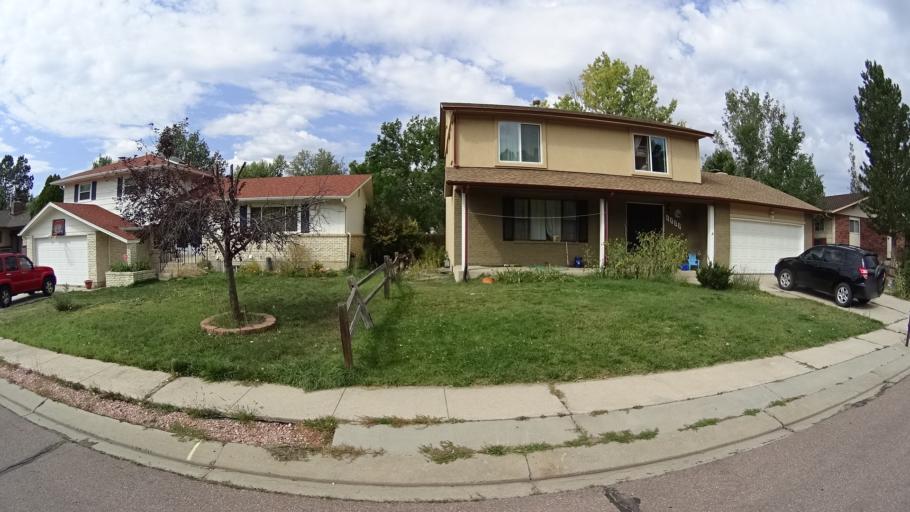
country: US
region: Colorado
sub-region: El Paso County
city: Cimarron Hills
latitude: 38.8584
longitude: -104.7317
